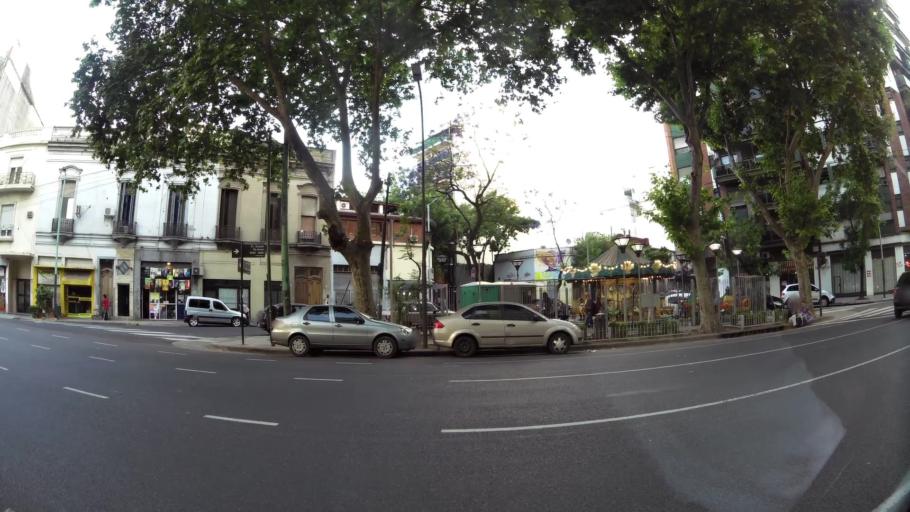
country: AR
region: Buenos Aires F.D.
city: Colegiales
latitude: -34.5996
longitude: -58.4299
